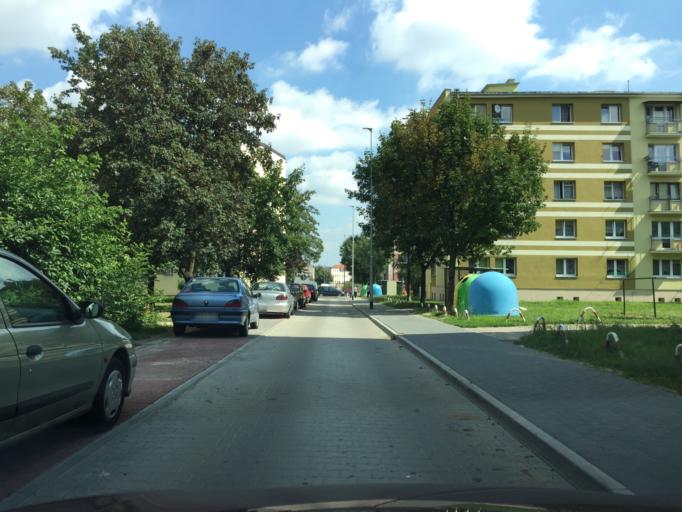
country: PL
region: Greater Poland Voivodeship
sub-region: Kalisz
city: Kalisz
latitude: 51.7497
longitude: 18.0730
